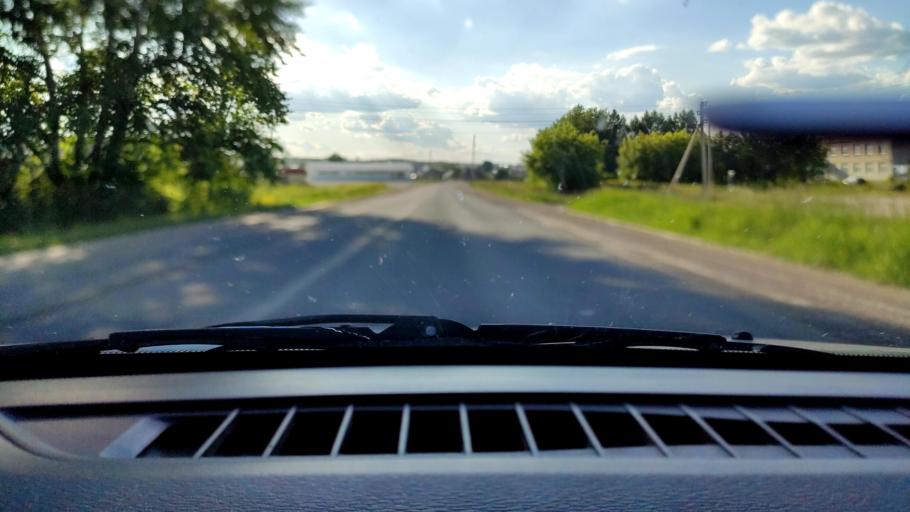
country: RU
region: Perm
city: Orda
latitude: 57.1898
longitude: 56.9084
